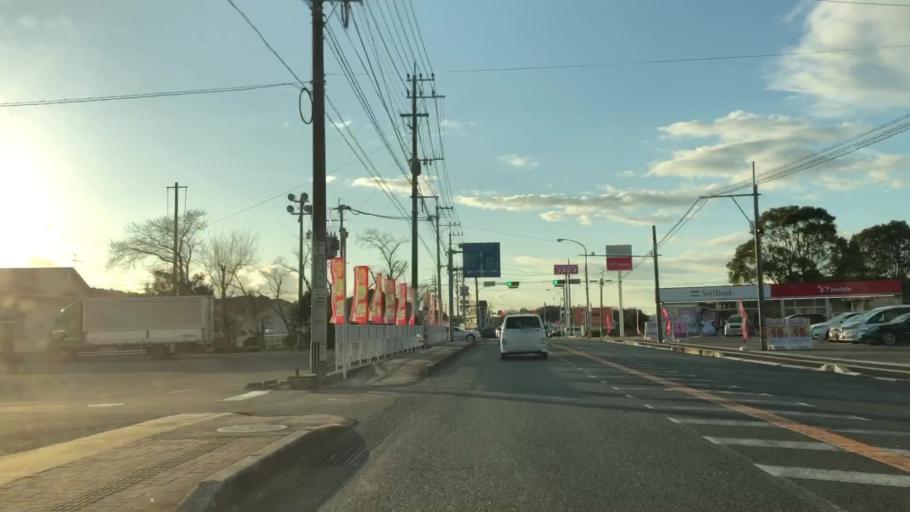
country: JP
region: Oita
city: Bungo-Takada-shi
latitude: 33.5348
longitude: 131.3250
